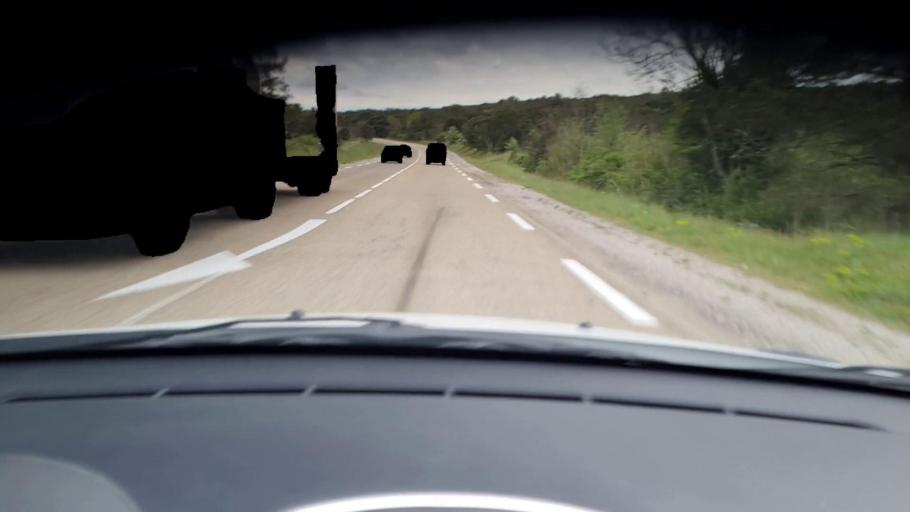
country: FR
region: Languedoc-Roussillon
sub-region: Departement du Gard
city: Poulx
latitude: 43.9154
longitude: 4.3874
